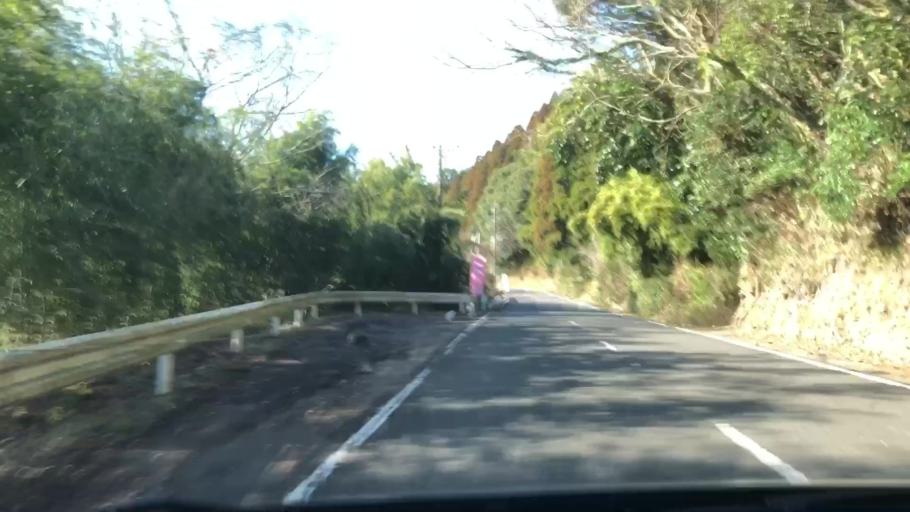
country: JP
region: Kagoshima
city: Satsumasendai
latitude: 31.8578
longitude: 130.3599
